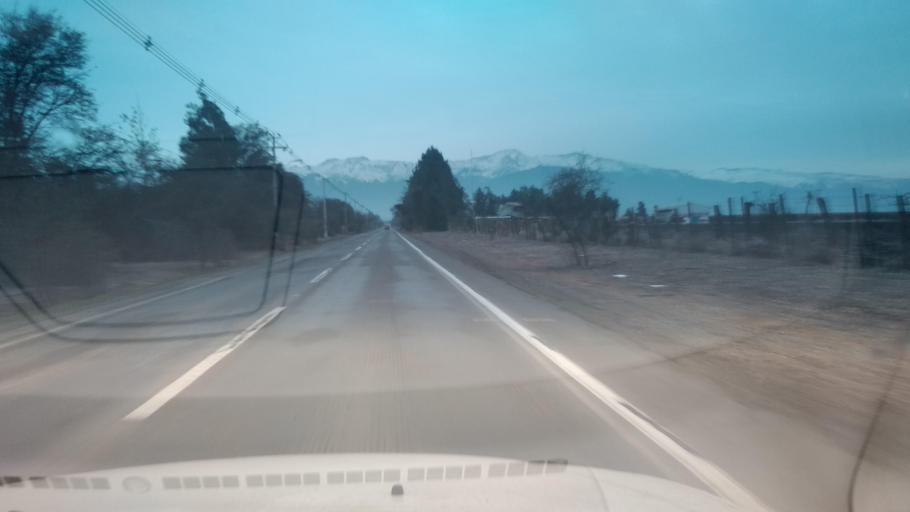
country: CL
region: Santiago Metropolitan
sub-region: Provincia de Chacabuco
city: Chicureo Abajo
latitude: -33.0934
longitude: -70.7128
